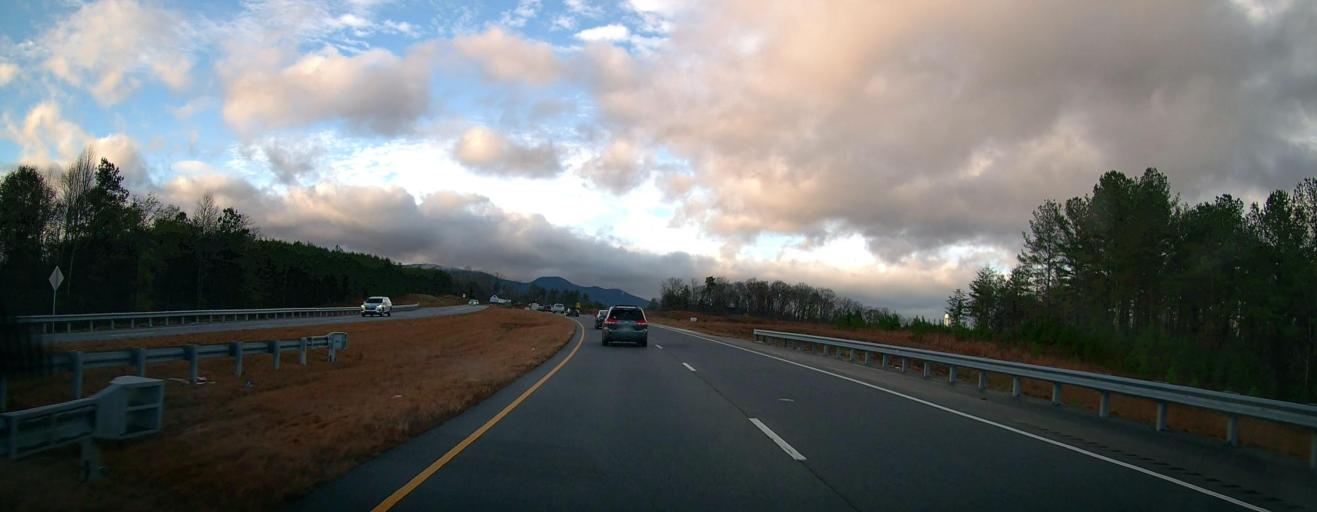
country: US
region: Georgia
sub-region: White County
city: Cleveland
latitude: 34.6006
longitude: -83.7807
